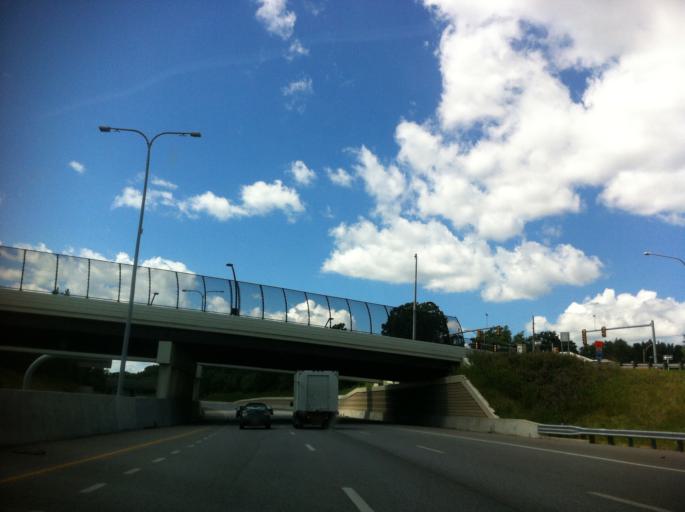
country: US
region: Ohio
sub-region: Lucas County
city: Ottawa Hills
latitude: 41.6850
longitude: -83.6032
